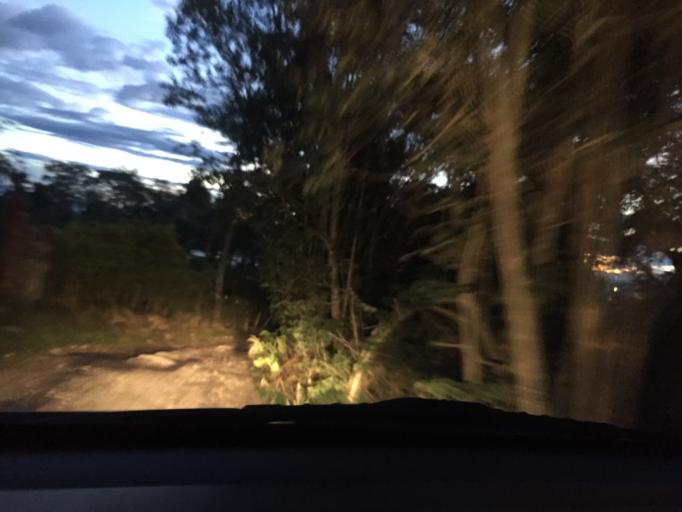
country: CO
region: Cundinamarca
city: Zipacon
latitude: 4.7221
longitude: -74.4223
